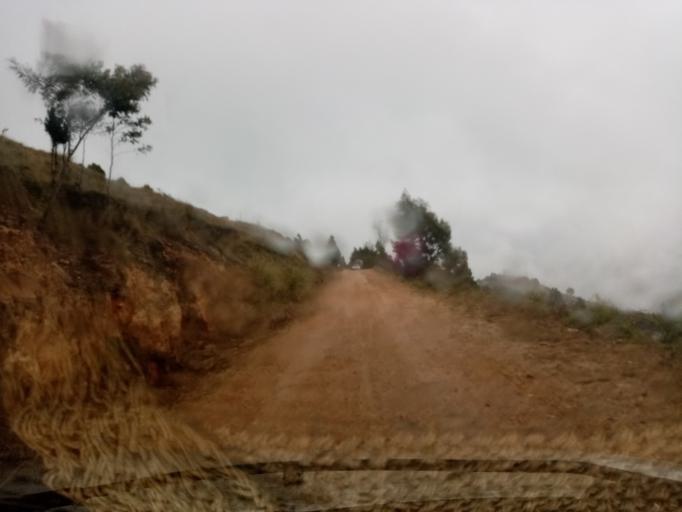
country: CO
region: Boyaca
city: Siachoque
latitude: 5.5538
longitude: -73.2811
